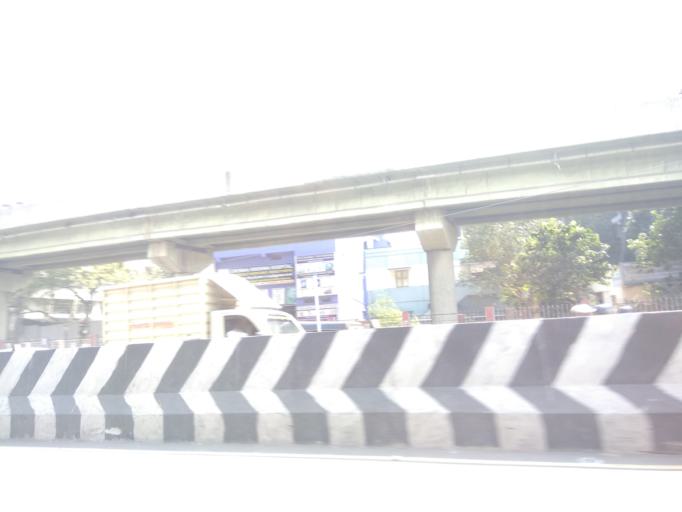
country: IN
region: Tamil Nadu
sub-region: Kancheepuram
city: Pallavaram
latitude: 12.9465
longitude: 80.1365
